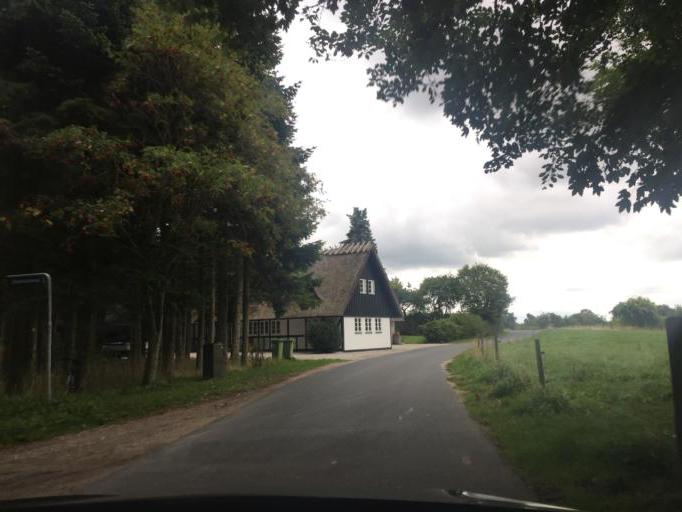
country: DK
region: South Denmark
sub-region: Assens Kommune
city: Tommerup
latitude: 55.3573
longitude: 10.2253
